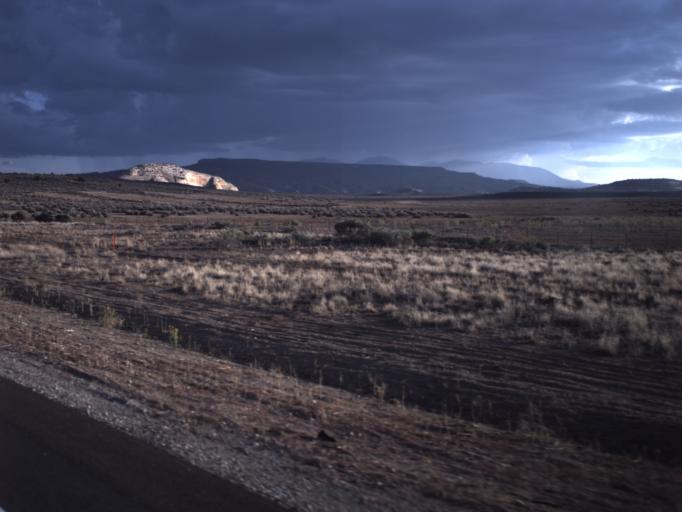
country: US
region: Utah
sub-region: San Juan County
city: Monticello
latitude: 38.0852
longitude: -109.3546
